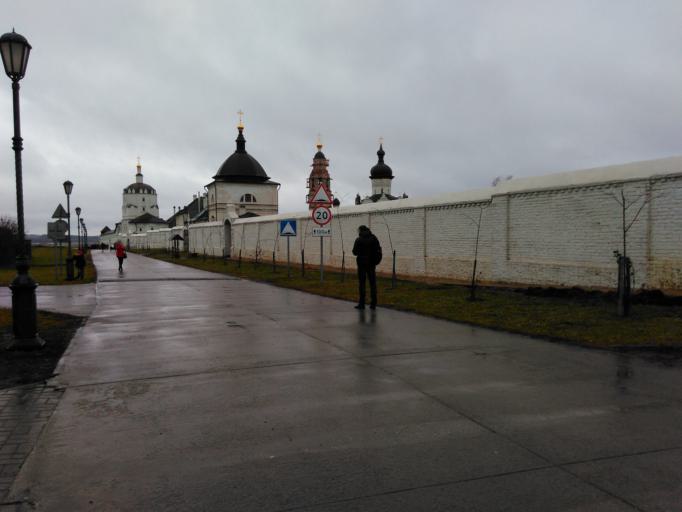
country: RU
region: Tatarstan
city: Sviyazhsk
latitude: 55.7707
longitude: 48.6554
